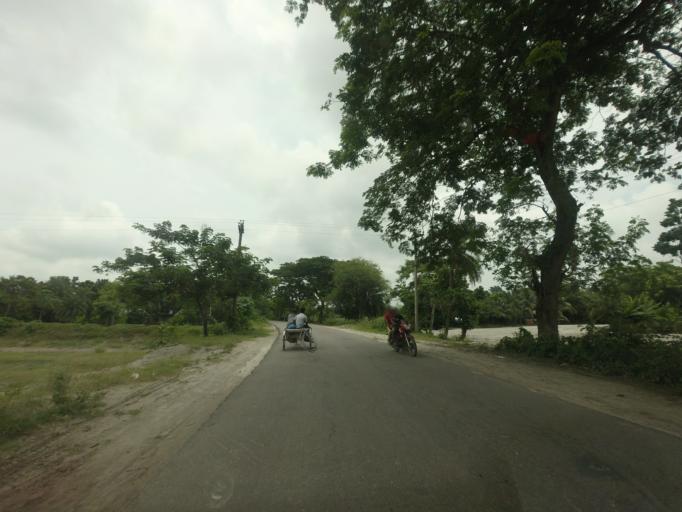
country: BD
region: Khulna
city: Kalia
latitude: 23.2106
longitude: 89.7090
